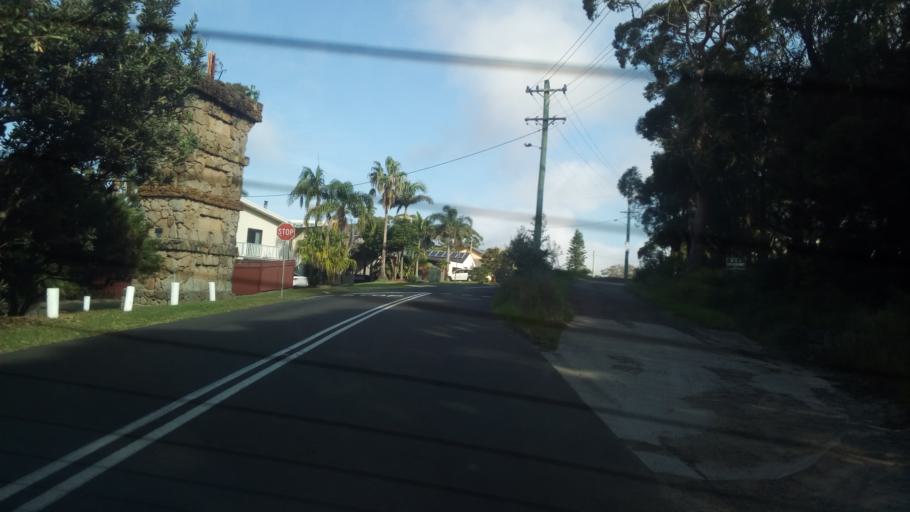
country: AU
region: New South Wales
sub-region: Wollongong
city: Helensburgh
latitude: -34.2188
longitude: 150.9788
